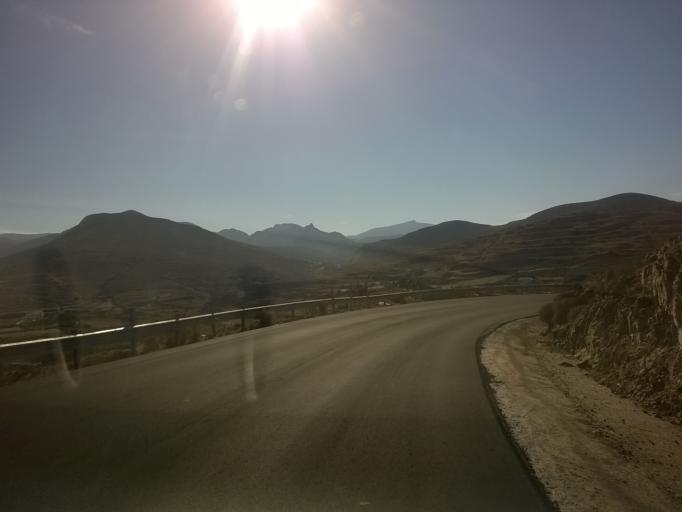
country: GR
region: South Aegean
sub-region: Nomos Kykladon
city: Naxos
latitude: 37.1173
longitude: 25.4211
